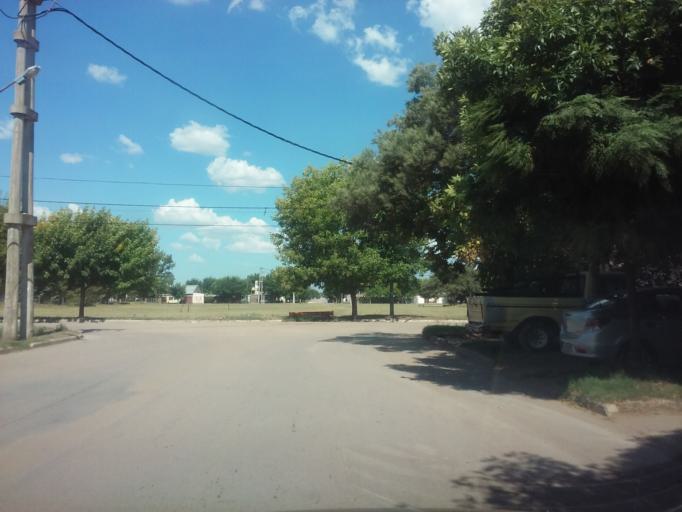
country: AR
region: La Pampa
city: Santa Rosa
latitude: -36.6427
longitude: -64.2984
